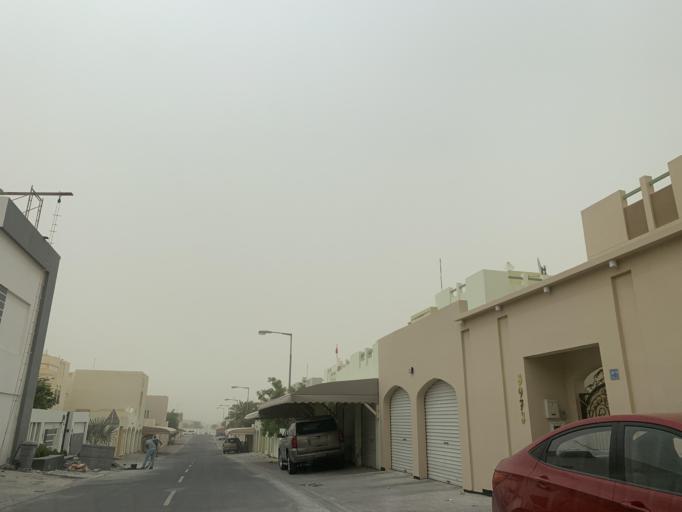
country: BH
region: Central Governorate
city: Madinat Hamad
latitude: 26.1269
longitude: 50.5096
